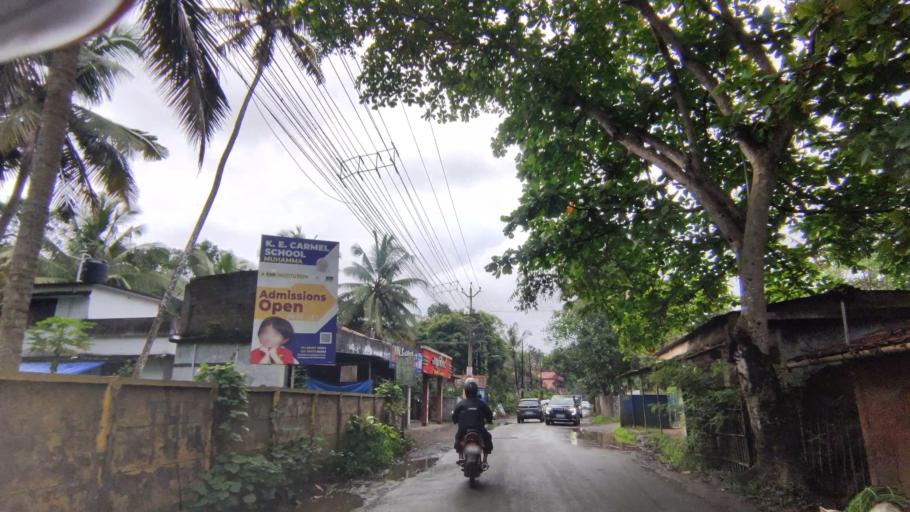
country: IN
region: Kerala
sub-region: Alappuzha
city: Shertallai
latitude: 9.6734
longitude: 76.4218
